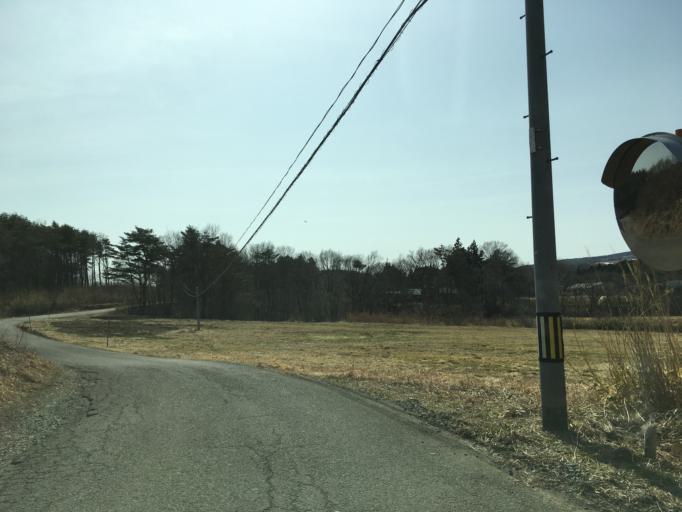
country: JP
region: Fukushima
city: Nihommatsu
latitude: 37.6263
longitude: 140.3602
